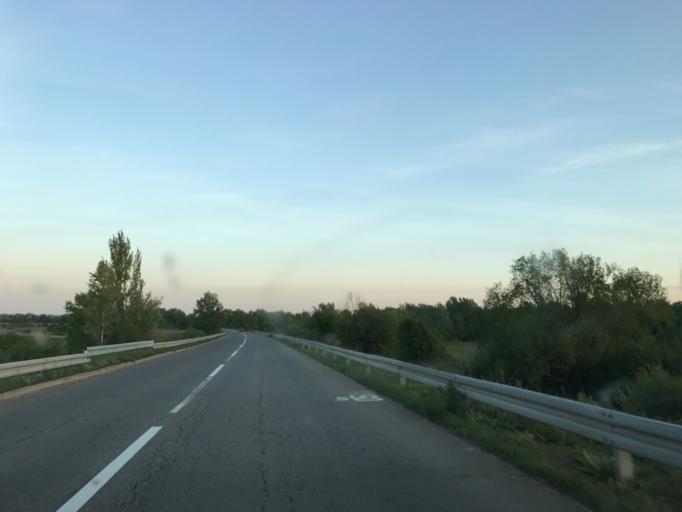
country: RS
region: Central Serbia
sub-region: Borski Okrug
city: Negotin
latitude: 44.2753
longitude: 22.5085
